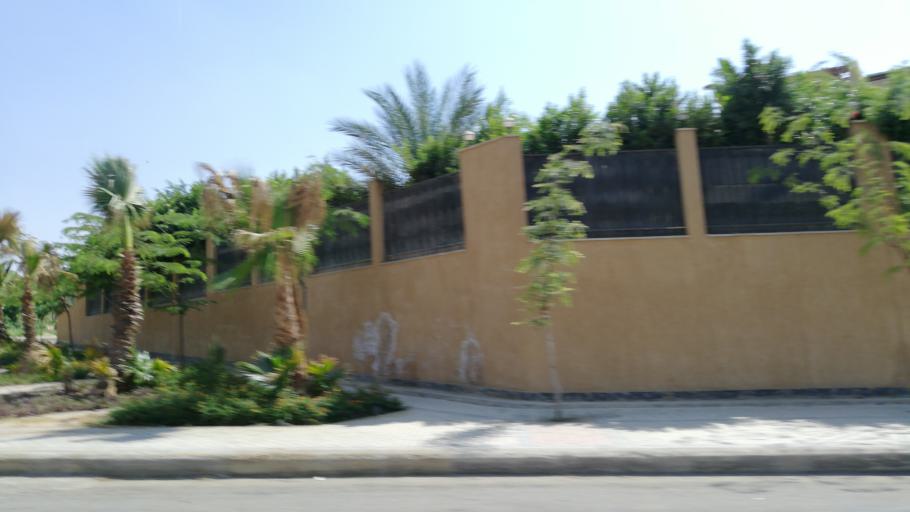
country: EG
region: Muhafazat al Qalyubiyah
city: Al Khankah
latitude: 30.0532
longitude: 31.4938
